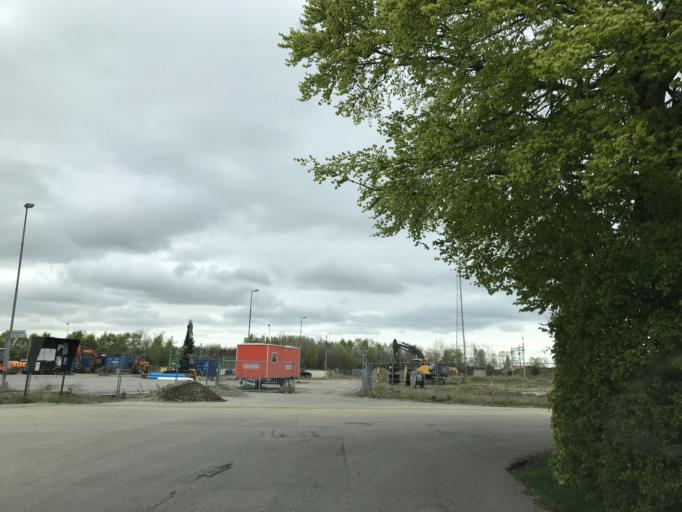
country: SE
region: Skane
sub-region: Svalovs Kommun
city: Teckomatorp
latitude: 55.8690
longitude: 13.0806
